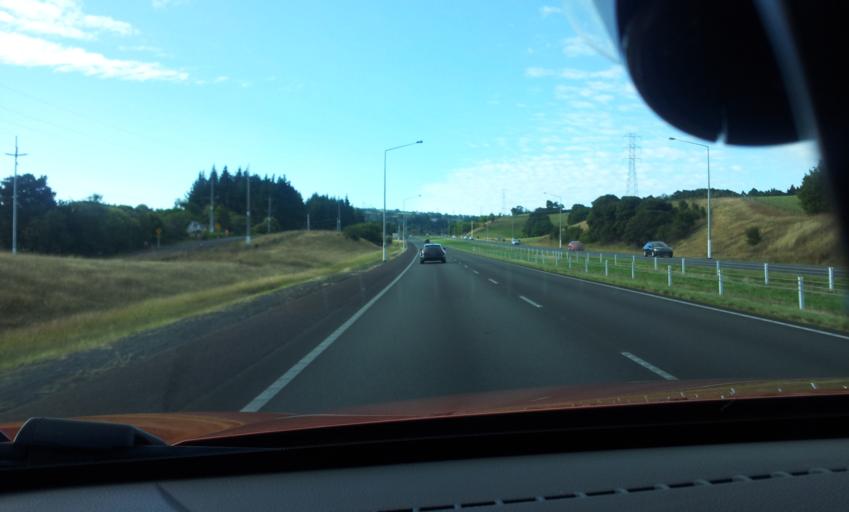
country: NZ
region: Auckland
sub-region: Auckland
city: Pukekohe East
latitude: -37.1572
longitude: 174.9783
